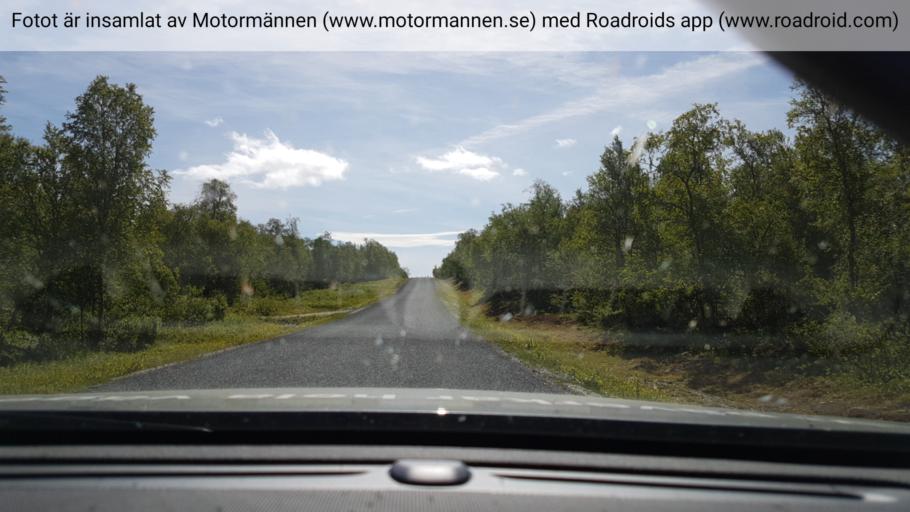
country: NO
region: Nordland
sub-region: Hattfjelldal
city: Hattfjelldal
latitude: 65.4165
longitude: 14.9264
